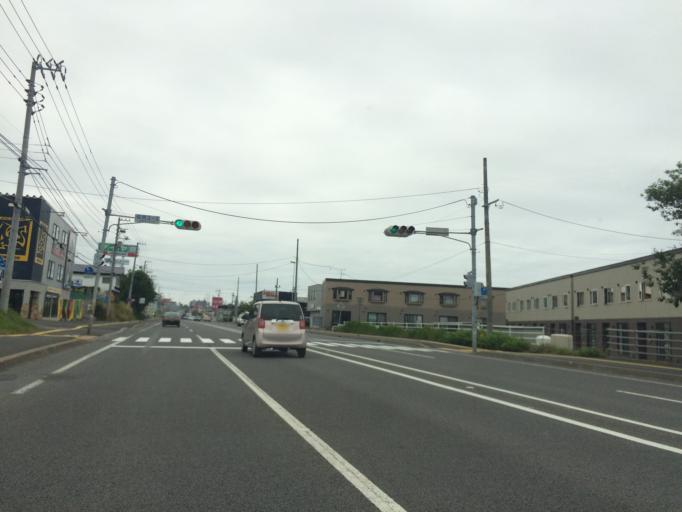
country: JP
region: Hokkaido
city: Sapporo
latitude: 43.1224
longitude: 141.2271
